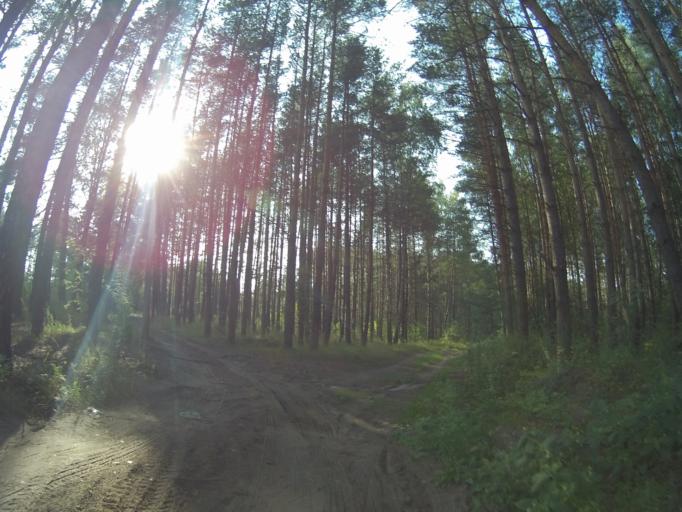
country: RU
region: Vladimir
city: Kommunar
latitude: 56.0669
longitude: 40.4418
